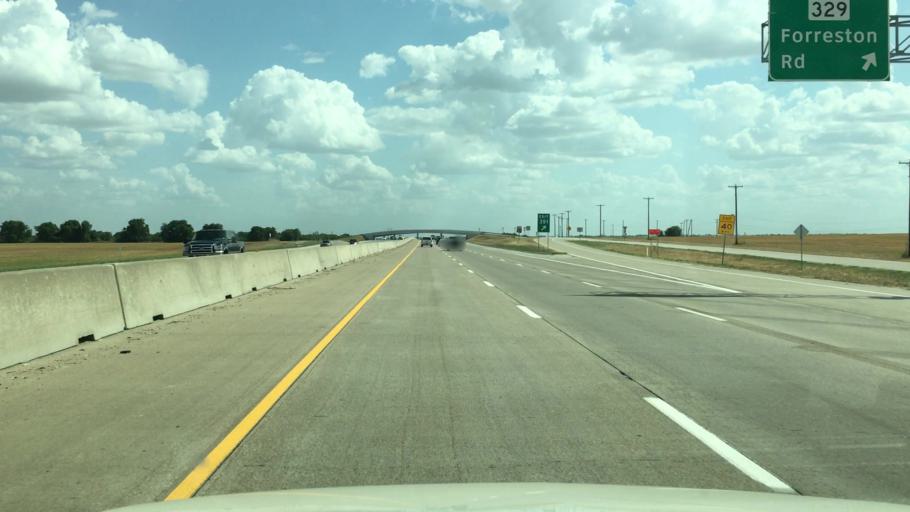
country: US
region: Texas
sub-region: Ellis County
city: Nash
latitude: 32.2658
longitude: -96.8717
